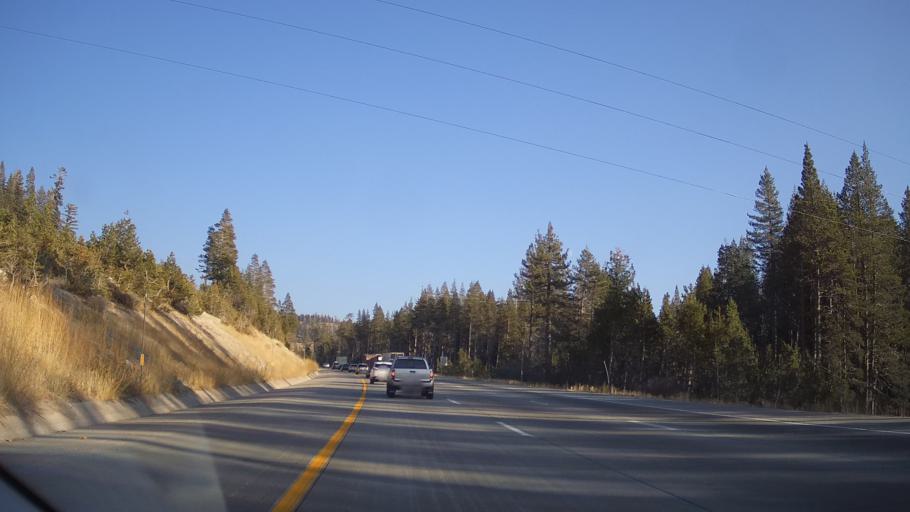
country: US
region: California
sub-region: Nevada County
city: Truckee
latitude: 39.3266
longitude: -120.3816
